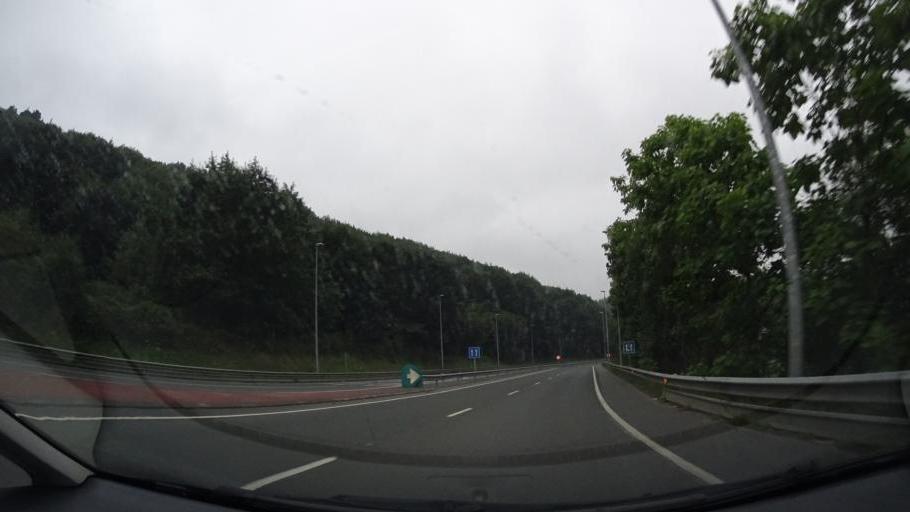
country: ES
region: Basque Country
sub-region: Bizkaia
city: Durango
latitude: 43.1668
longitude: -2.6416
